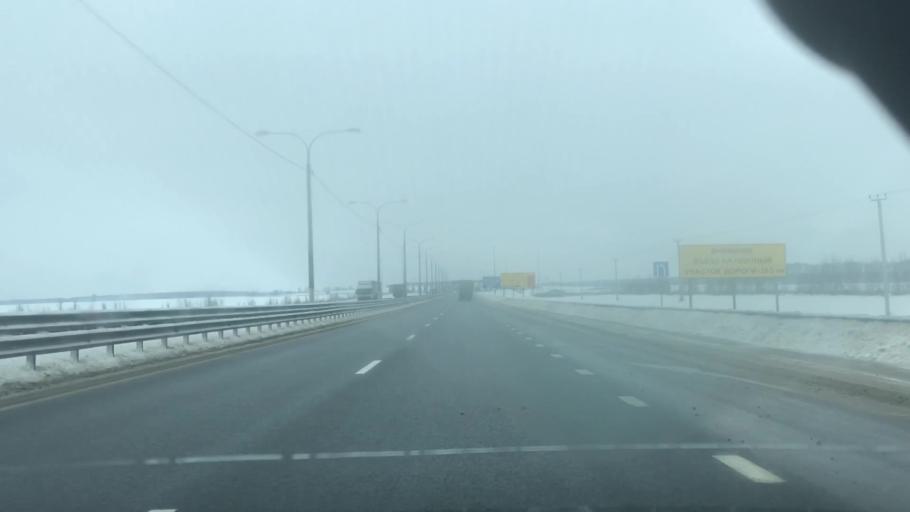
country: RU
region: Tula
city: Dubovka
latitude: 53.8845
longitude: 38.0515
